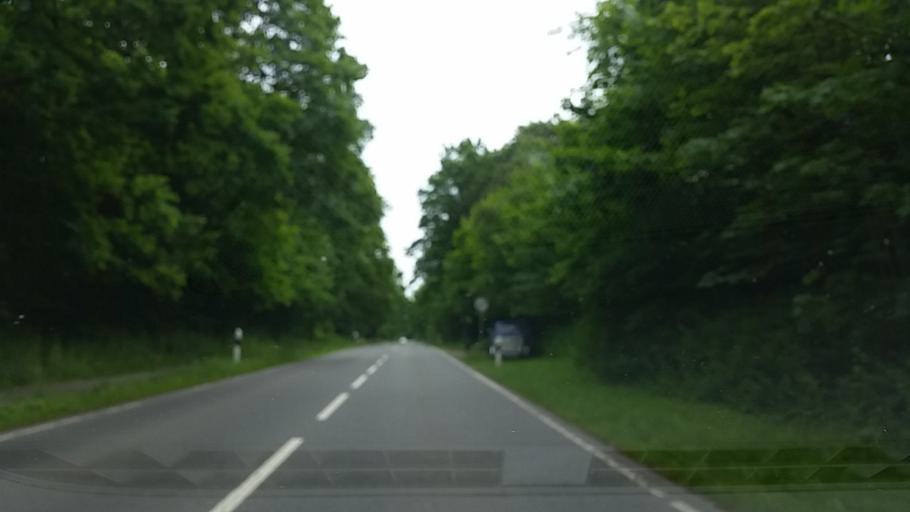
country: DE
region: Schleswig-Holstein
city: Kuddeworde
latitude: 53.5915
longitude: 10.3963
